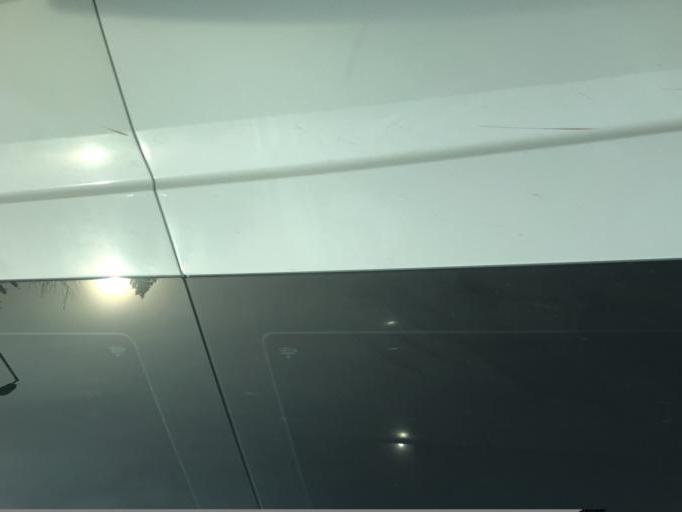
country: TR
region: Istanbul
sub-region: Atasehir
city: Atasehir
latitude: 40.9500
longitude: 29.1229
